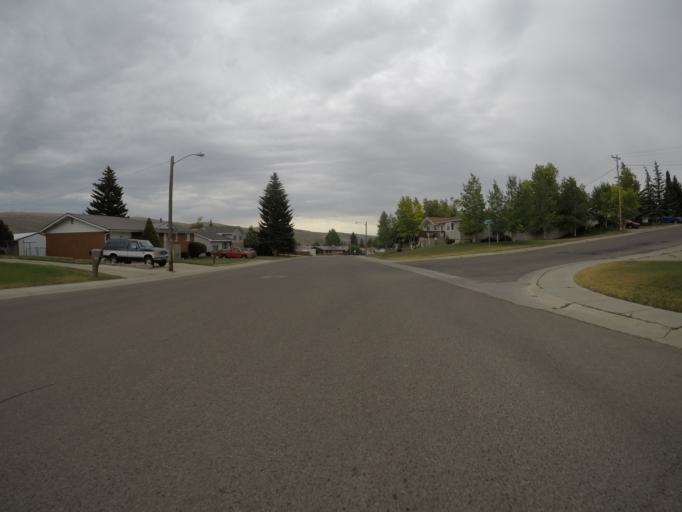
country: US
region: Wyoming
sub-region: Lincoln County
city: Kemmerer
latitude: 41.7902
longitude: -110.5438
